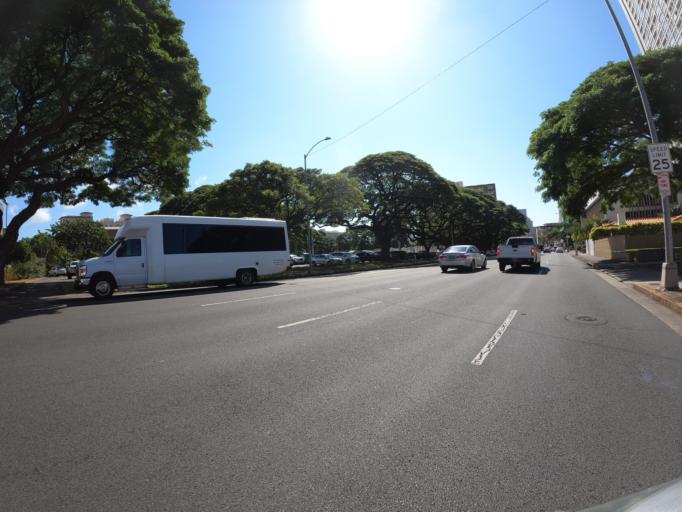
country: US
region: Hawaii
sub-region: Honolulu County
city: Honolulu
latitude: 21.2999
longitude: -157.8345
